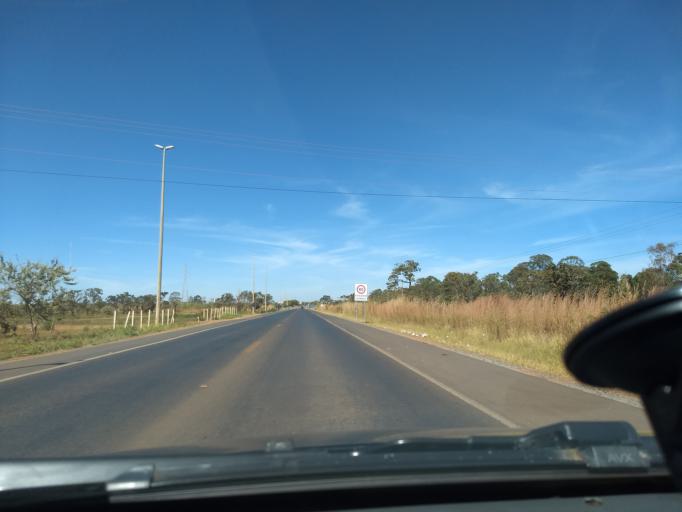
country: BR
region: Federal District
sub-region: Brasilia
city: Brasilia
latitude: -15.7833
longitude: -48.0497
